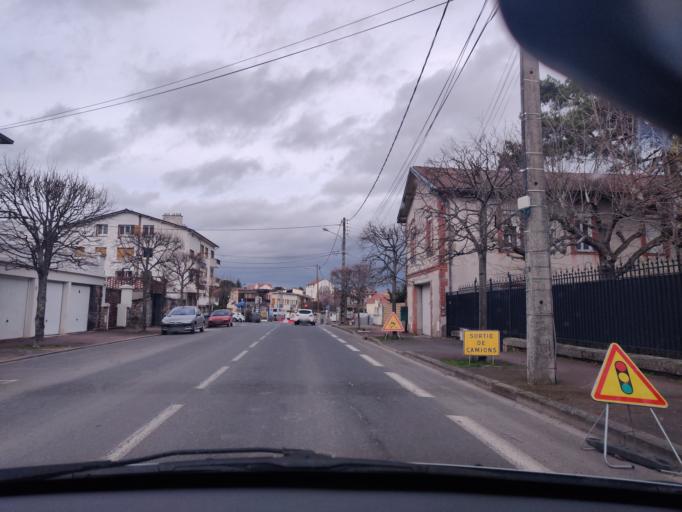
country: FR
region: Auvergne
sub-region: Departement du Puy-de-Dome
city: Chatel-Guyon
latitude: 45.9215
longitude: 3.0619
